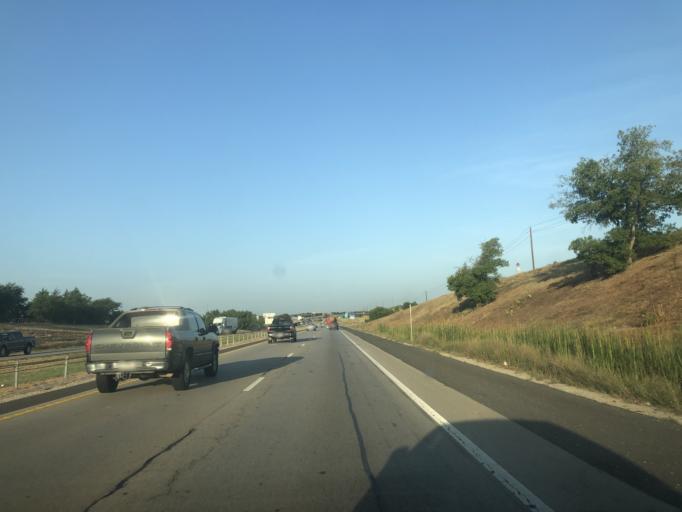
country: US
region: Texas
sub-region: Tarrant County
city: White Settlement
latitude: 32.7287
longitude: -97.5061
